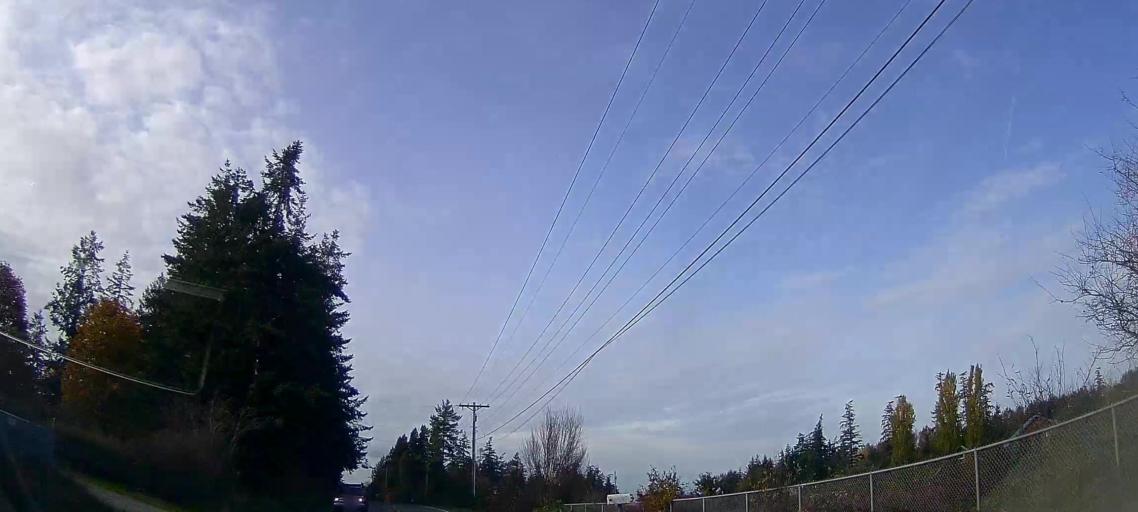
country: US
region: Washington
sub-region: Snohomish County
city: Stanwood
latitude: 48.2492
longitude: -122.4624
